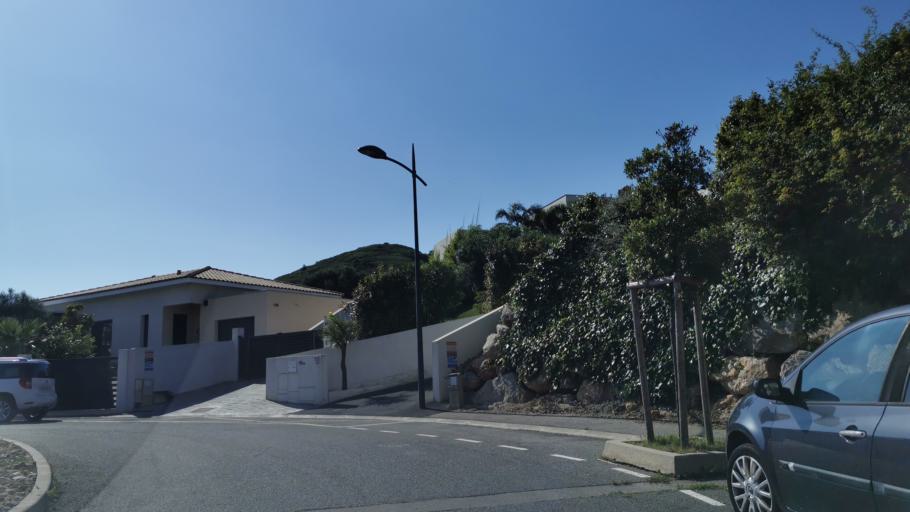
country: FR
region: Languedoc-Roussillon
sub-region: Departement de l'Aude
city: Peyriac-de-Mer
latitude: 43.1353
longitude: 2.9579
